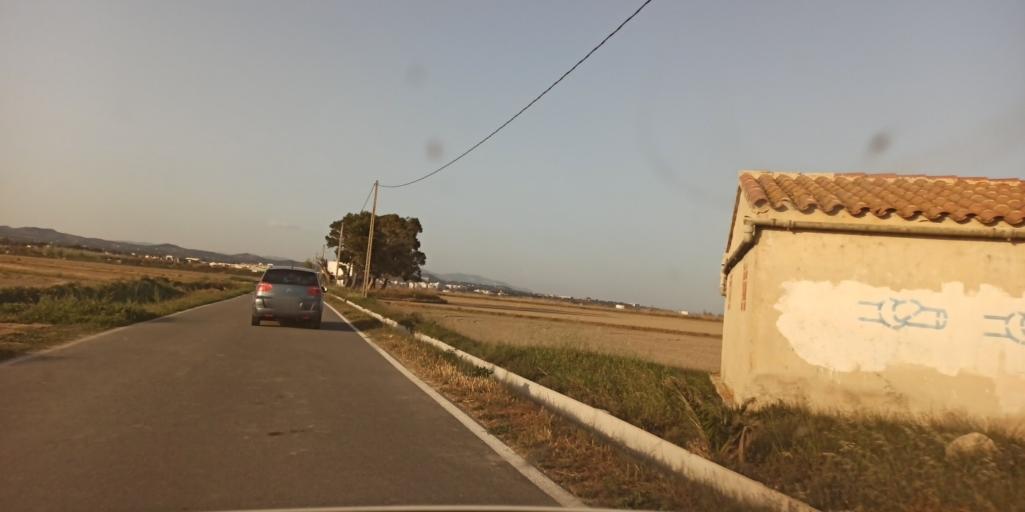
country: ES
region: Catalonia
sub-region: Provincia de Tarragona
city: L'Ampolla
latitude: 40.7917
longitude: 0.6981
